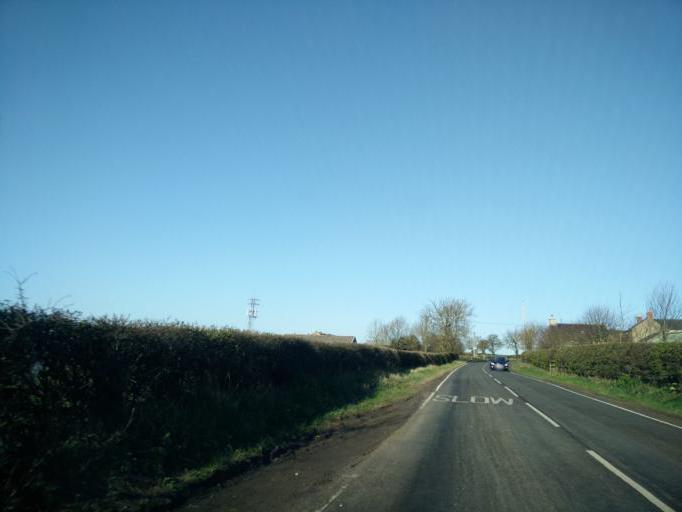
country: GB
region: England
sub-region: County Durham
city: Bishop Auckland
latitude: 54.6476
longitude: -1.7064
